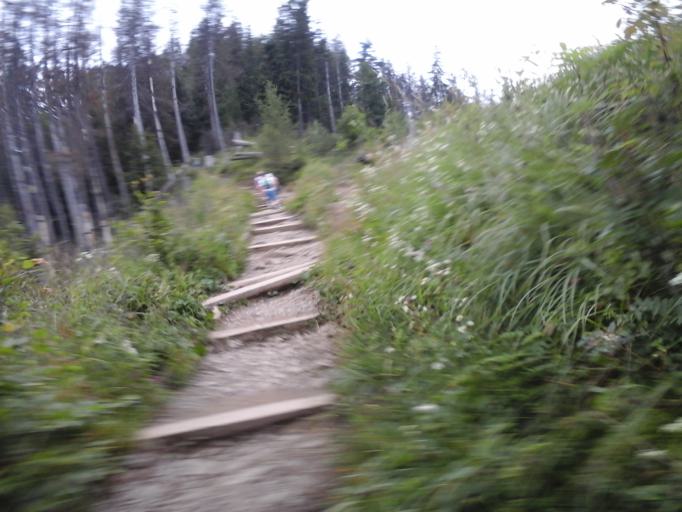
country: PL
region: Lesser Poland Voivodeship
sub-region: Powiat tatrzanski
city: Zakopane
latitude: 49.2753
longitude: 19.9900
